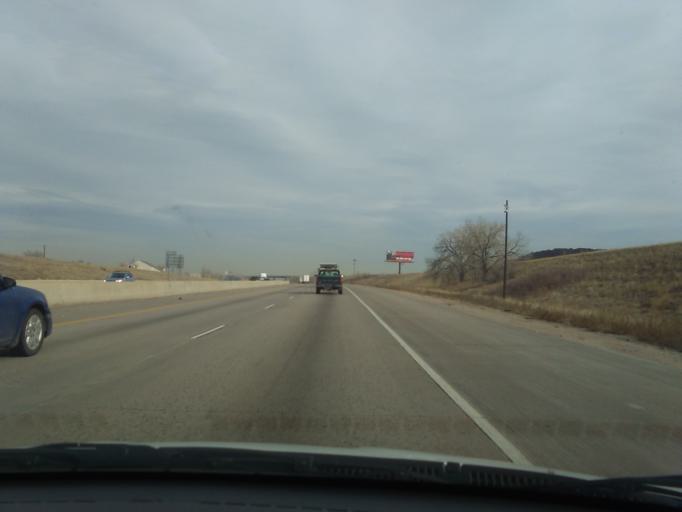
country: US
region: Colorado
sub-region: Adams County
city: Derby
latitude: 39.8391
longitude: -104.9314
